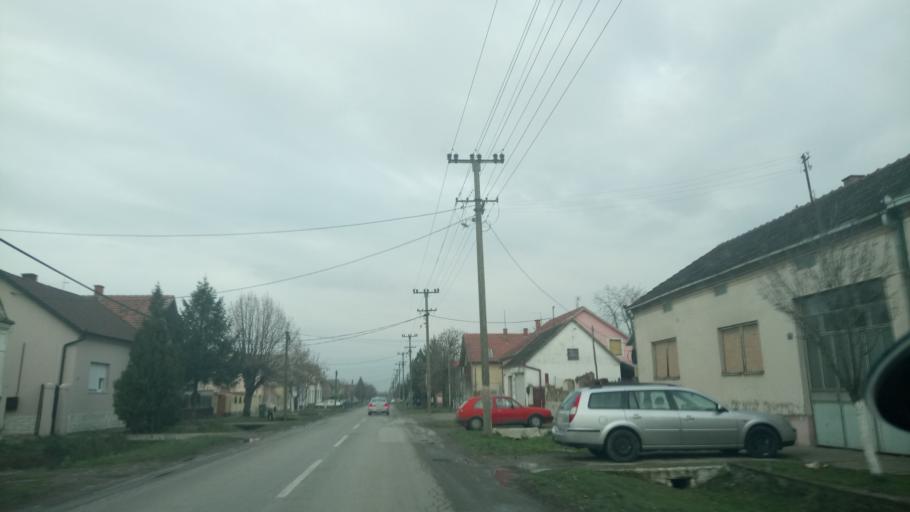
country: RS
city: Vojka
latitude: 44.9388
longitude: 20.1523
